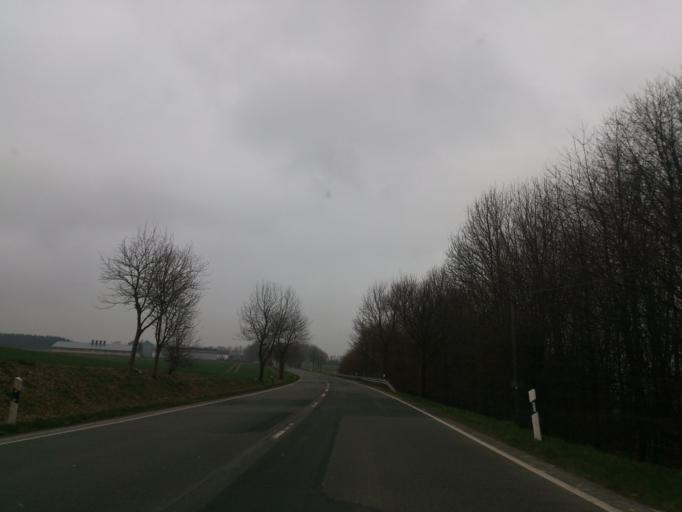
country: DE
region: North Rhine-Westphalia
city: Marsberg
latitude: 51.5487
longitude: 8.8370
